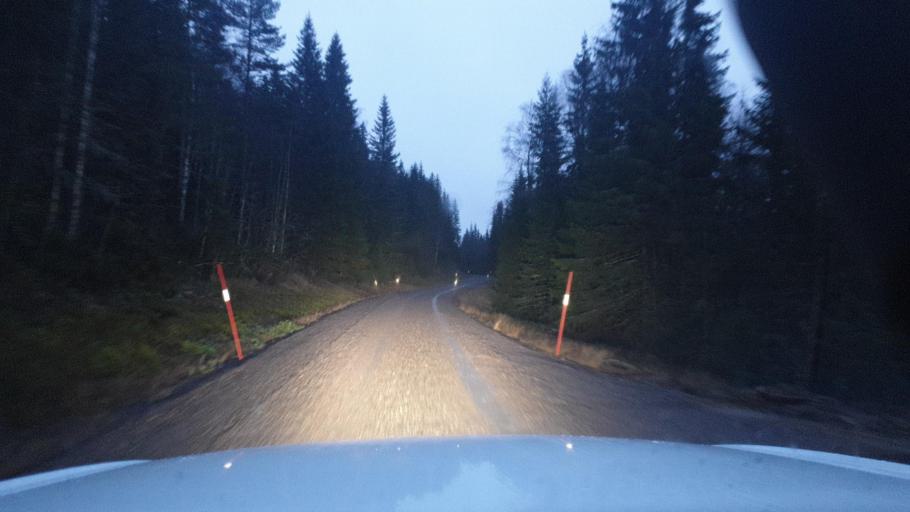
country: SE
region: Vaermland
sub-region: Eda Kommun
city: Charlottenberg
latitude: 60.0967
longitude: 12.6109
